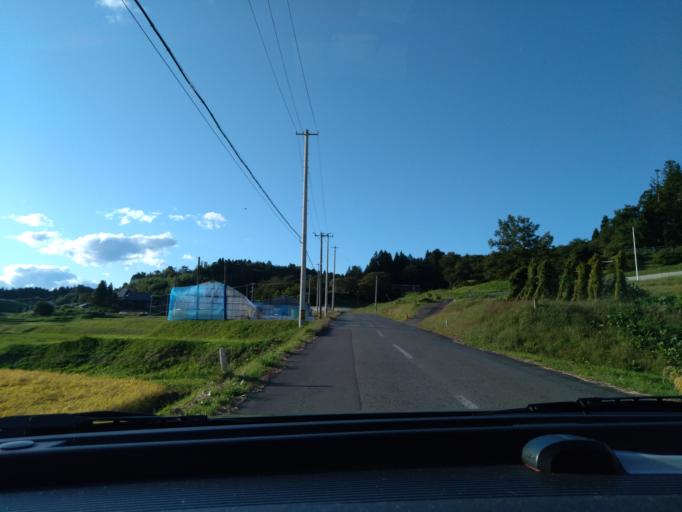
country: JP
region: Iwate
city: Ichinoseki
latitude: 38.8668
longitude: 141.1876
